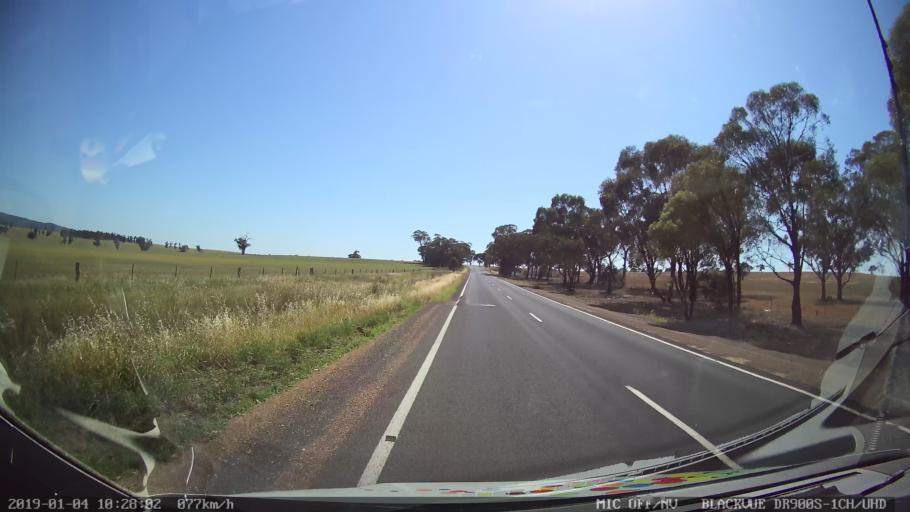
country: AU
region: New South Wales
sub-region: Cabonne
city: Canowindra
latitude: -33.3657
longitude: 148.6048
